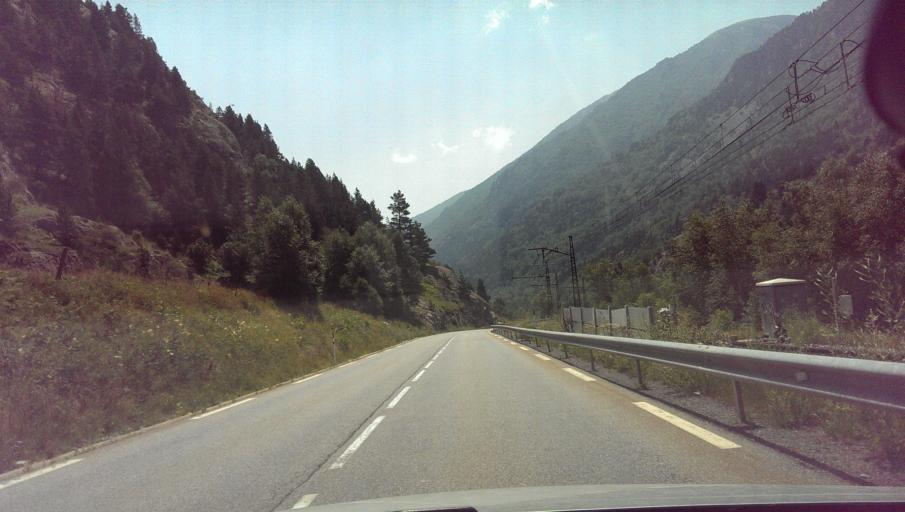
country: ES
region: Catalonia
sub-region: Provincia de Girona
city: Meranges
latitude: 42.5198
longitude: 1.8225
